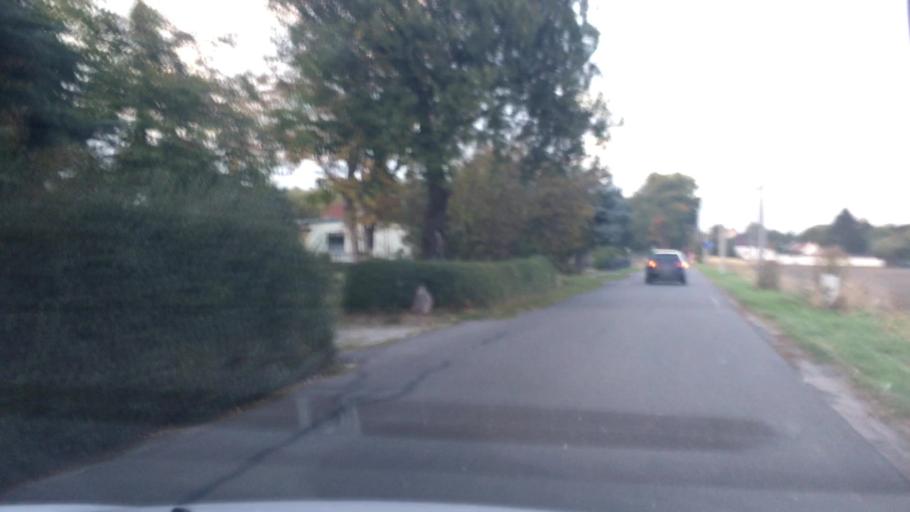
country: DE
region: Brandenburg
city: Welzow
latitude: 51.5689
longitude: 14.1654
